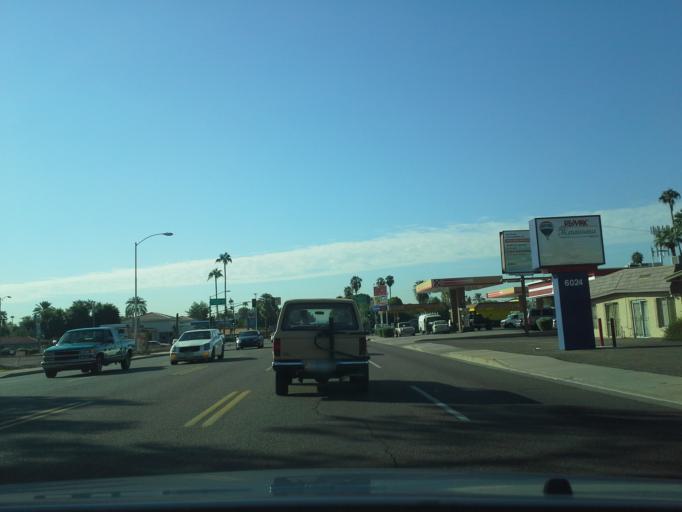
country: US
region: Arizona
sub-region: Maricopa County
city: Phoenix
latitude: 33.5250
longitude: -112.0825
